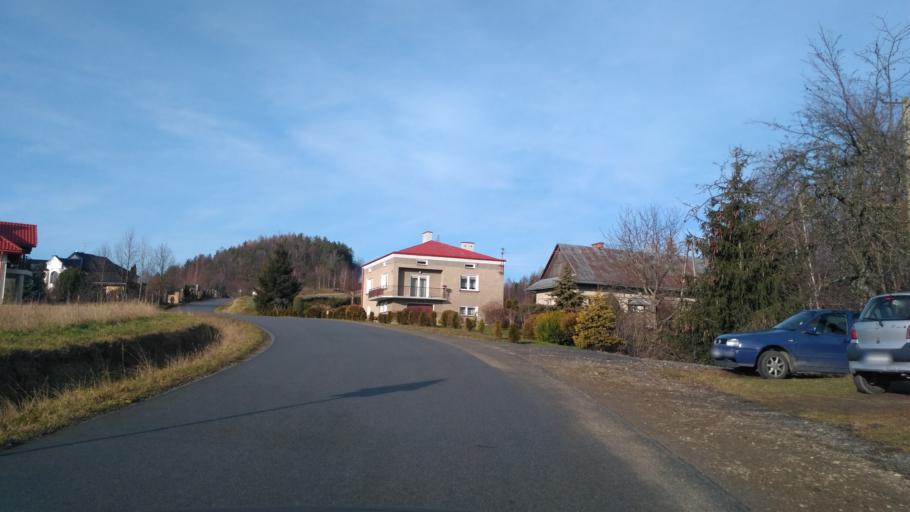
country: PL
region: Subcarpathian Voivodeship
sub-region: Powiat krosnienski
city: Korczyna
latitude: 49.7262
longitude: 21.7961
